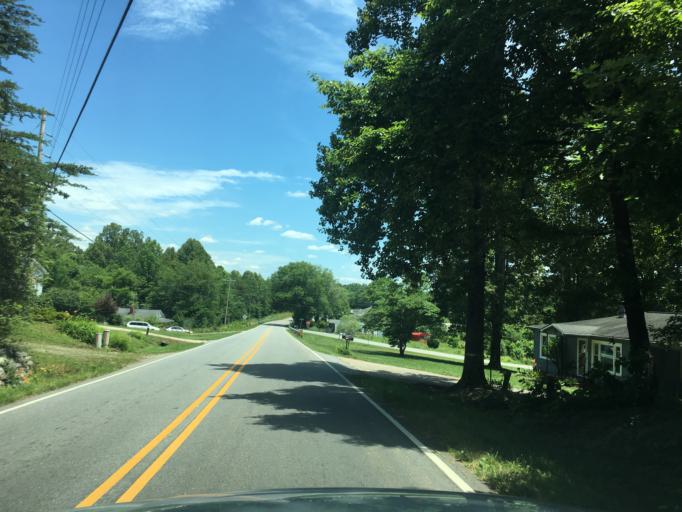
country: US
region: North Carolina
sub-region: Burke County
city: Glen Alpine
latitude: 35.6662
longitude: -81.7739
